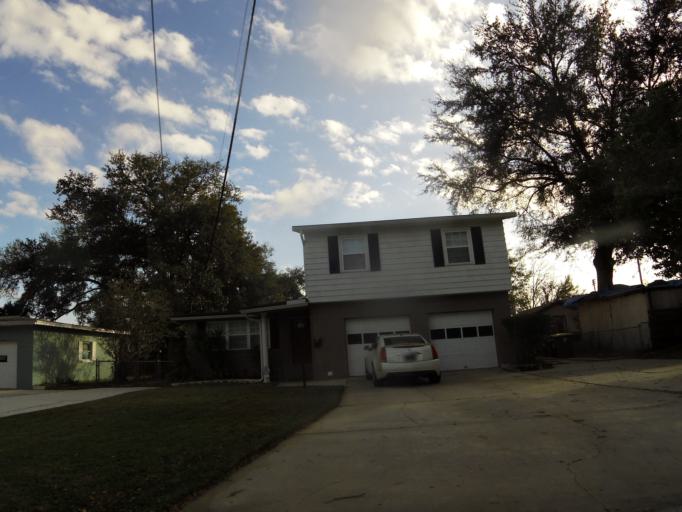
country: US
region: Florida
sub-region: Duval County
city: Jacksonville
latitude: 30.2801
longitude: -81.6120
